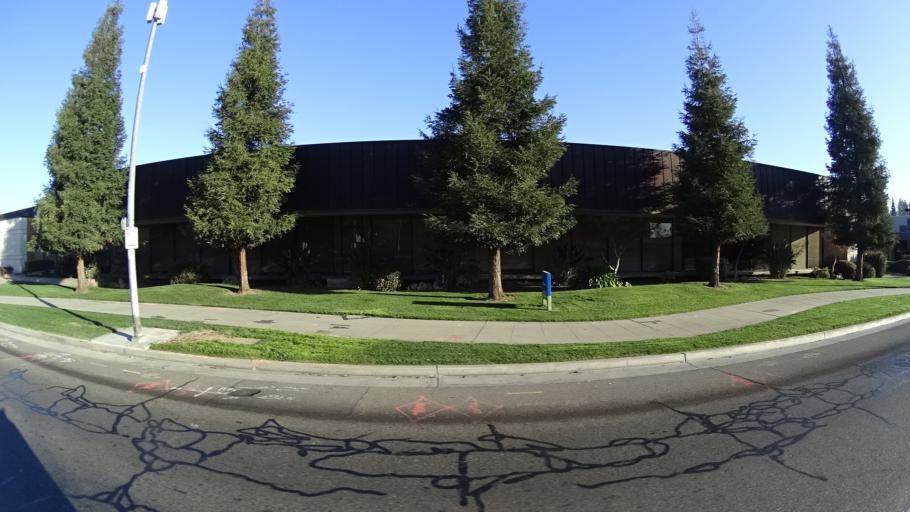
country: US
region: California
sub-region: Fresno County
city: Fresno
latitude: 36.8086
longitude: -119.7658
